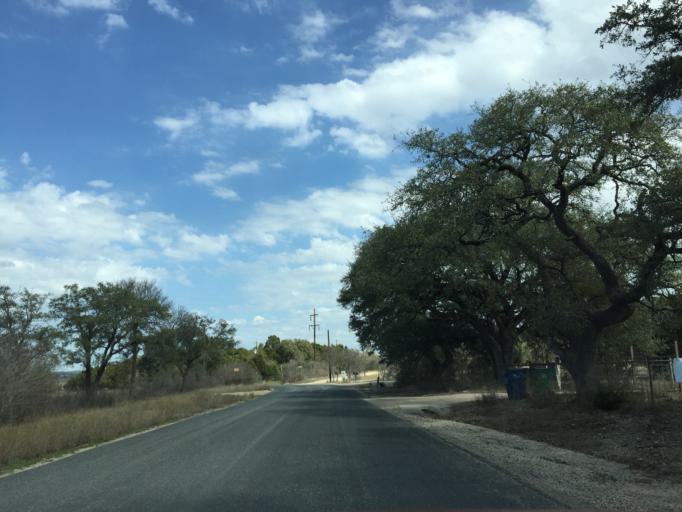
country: US
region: Texas
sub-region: Burnet County
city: Bertram
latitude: 30.7512
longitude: -97.9381
